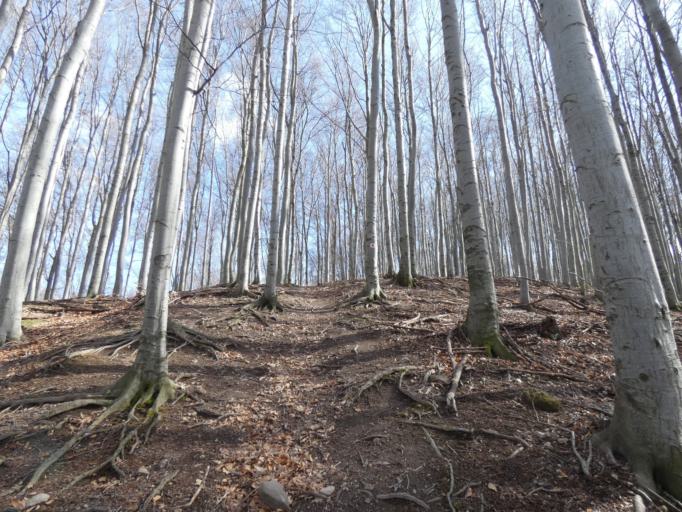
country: HU
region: Nograd
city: Diosjeno
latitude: 47.9742
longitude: 18.9549
